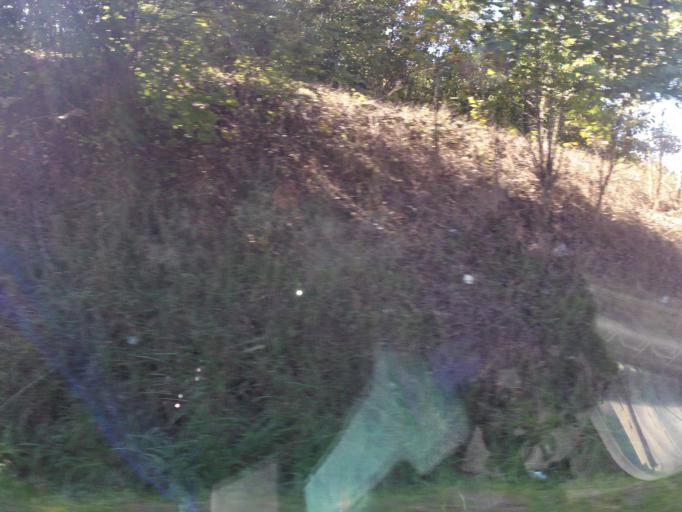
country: US
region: Kentucky
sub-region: Clay County
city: Manchester
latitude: 37.1356
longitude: -83.7600
